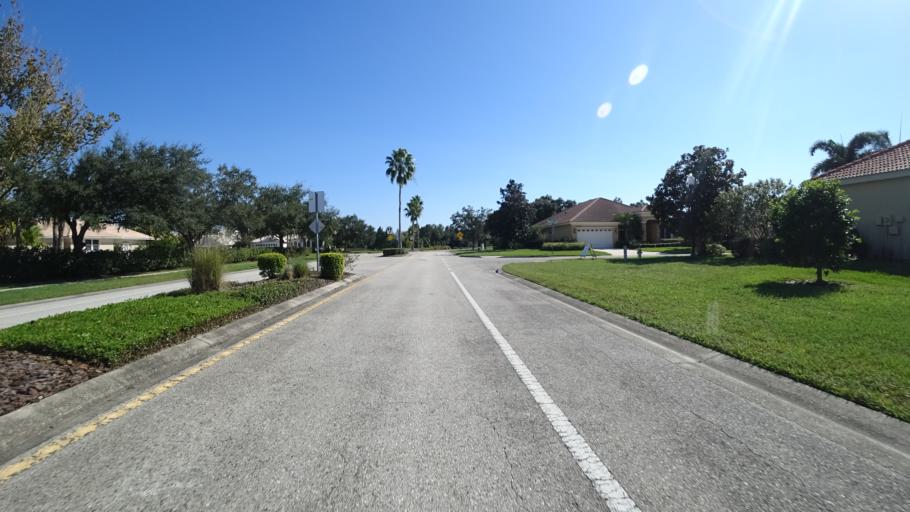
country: US
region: Florida
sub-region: Sarasota County
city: The Meadows
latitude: 27.4087
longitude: -82.4389
